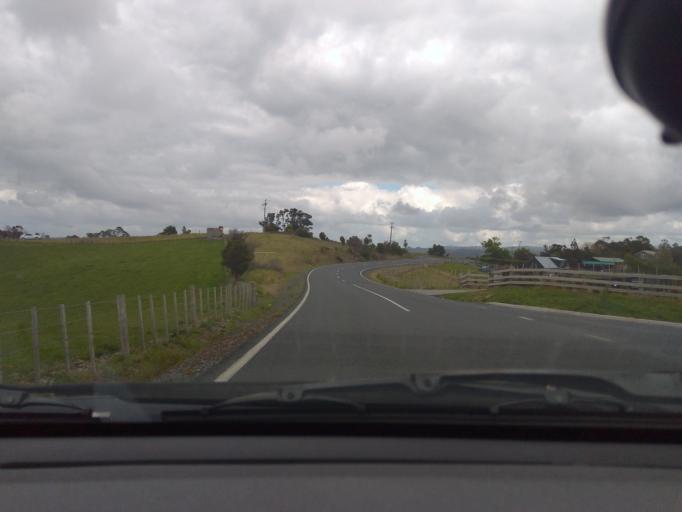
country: NZ
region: Auckland
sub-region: Auckland
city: Warkworth
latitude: -36.4455
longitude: 174.7511
